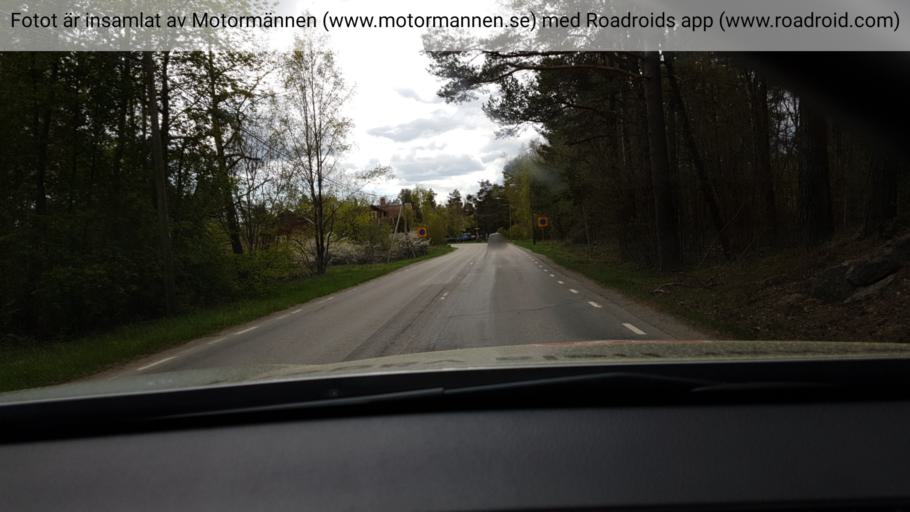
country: SE
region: Stockholm
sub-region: Haninge Kommun
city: Haninge
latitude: 59.0904
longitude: 18.1799
